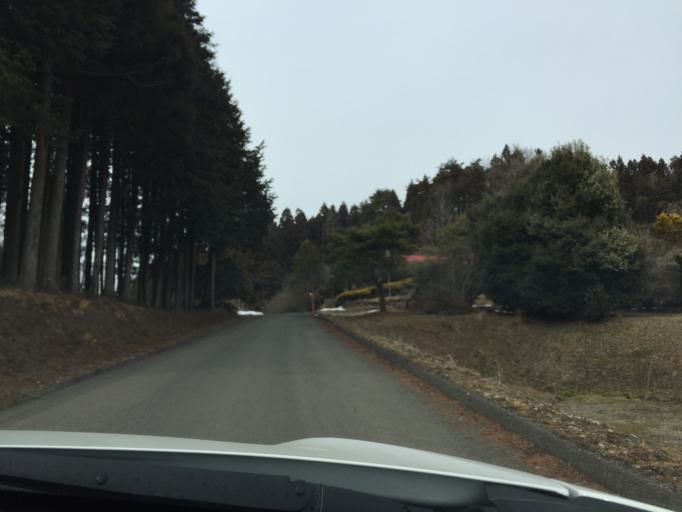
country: JP
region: Fukushima
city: Ishikawa
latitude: 37.1990
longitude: 140.5684
